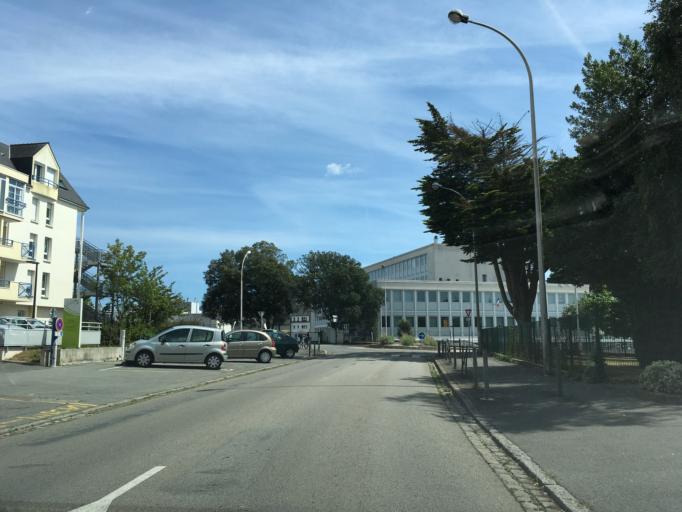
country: FR
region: Brittany
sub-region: Departement du Morbihan
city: Lorient
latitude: 47.7464
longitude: -3.3808
